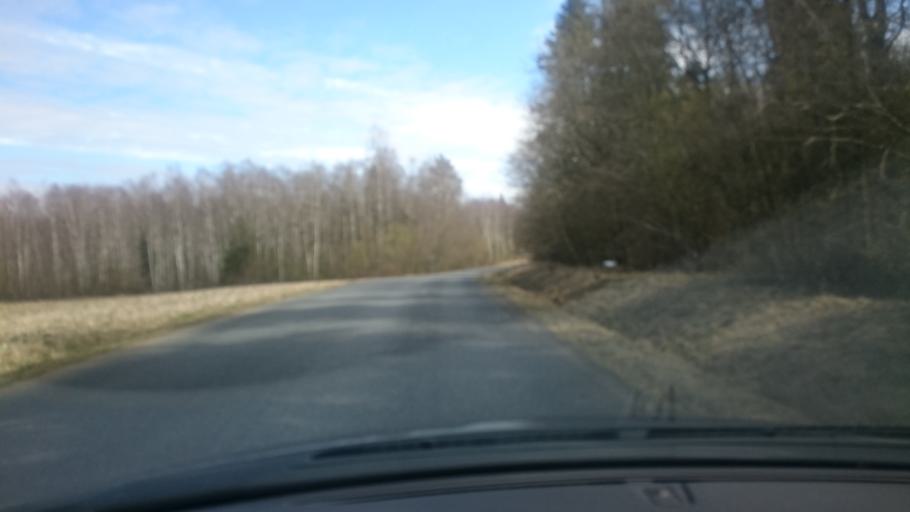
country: EE
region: Harju
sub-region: Anija vald
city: Kehra
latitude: 59.0961
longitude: 25.2671
